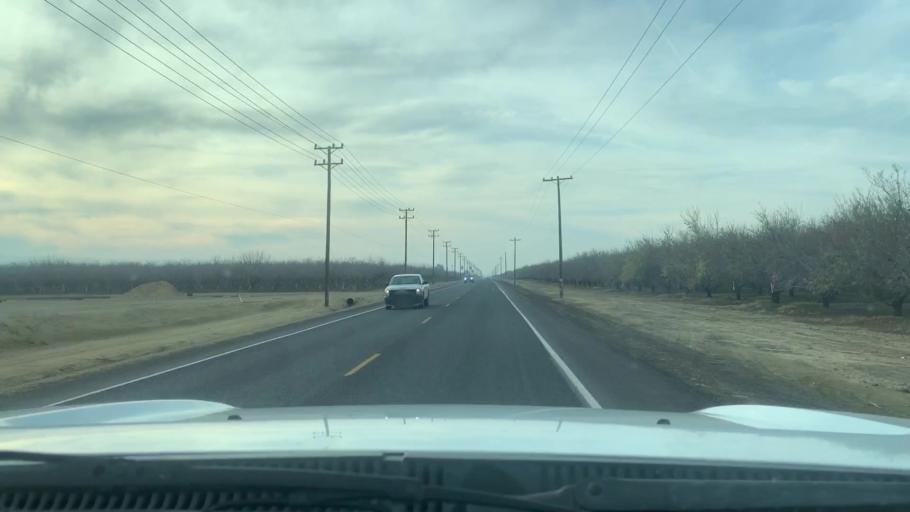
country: US
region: California
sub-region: Kern County
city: Lost Hills
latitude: 35.4993
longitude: -119.6572
